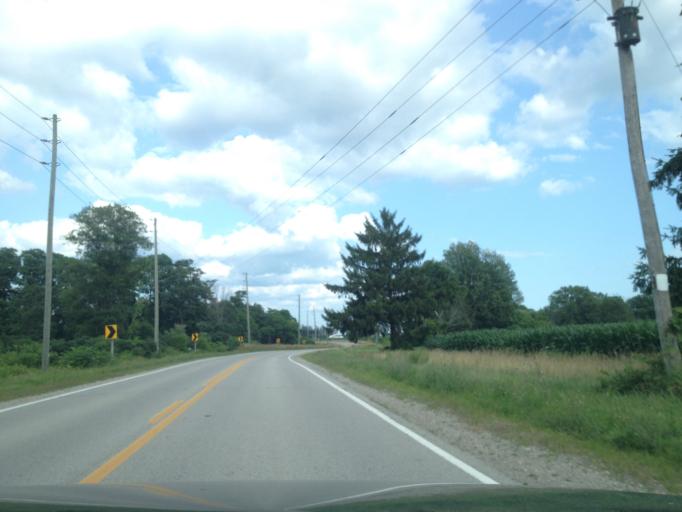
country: CA
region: Ontario
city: Aylmer
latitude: 42.6743
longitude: -80.9043
